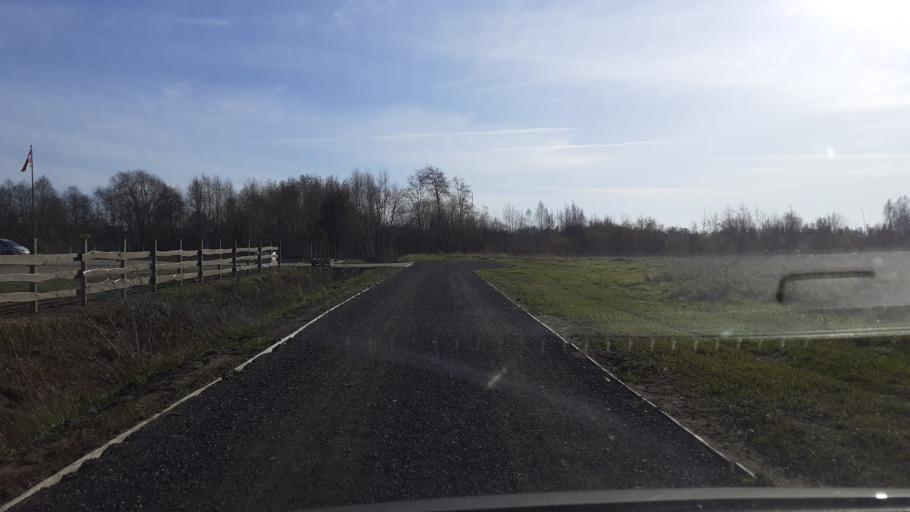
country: LV
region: Kuldigas Rajons
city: Kuldiga
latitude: 56.9573
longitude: 21.9972
